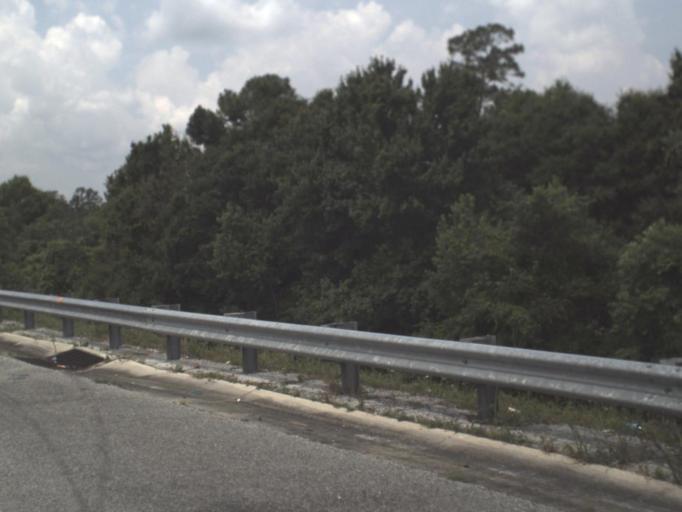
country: US
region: Florida
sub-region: Clay County
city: Green Cove Springs
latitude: 29.9570
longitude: -81.6716
